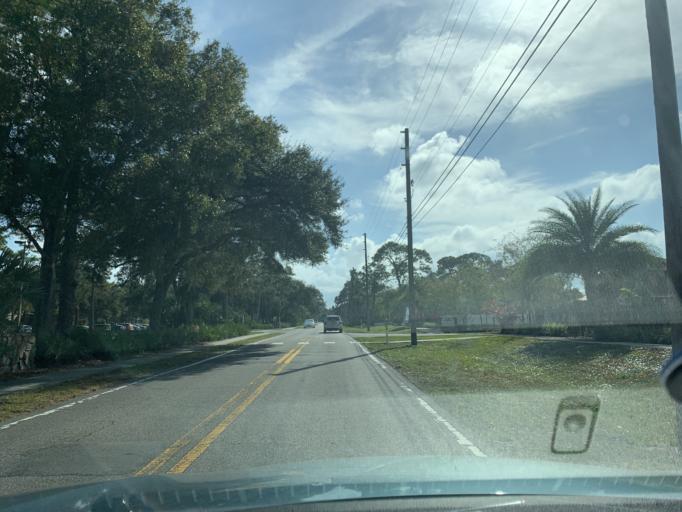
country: US
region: Florida
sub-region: Pinellas County
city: South Highpoint
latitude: 27.9195
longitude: -82.7136
